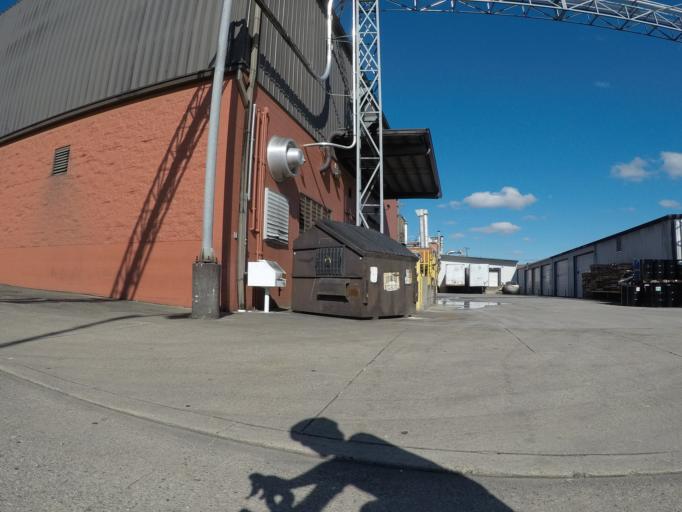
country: US
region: West Virginia
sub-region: Cabell County
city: Huntington
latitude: 38.4124
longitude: -82.4800
